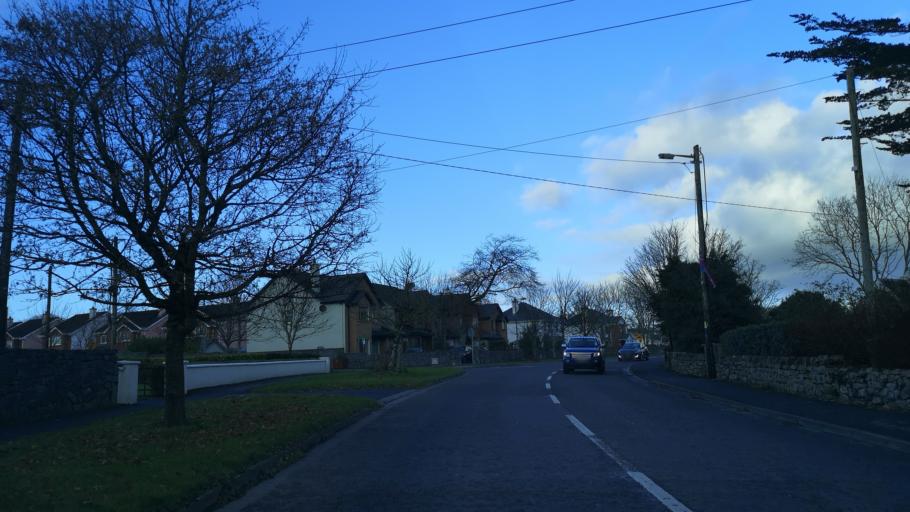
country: IE
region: Connaught
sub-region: County Galway
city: Oranmore
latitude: 53.2619
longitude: -8.9328
